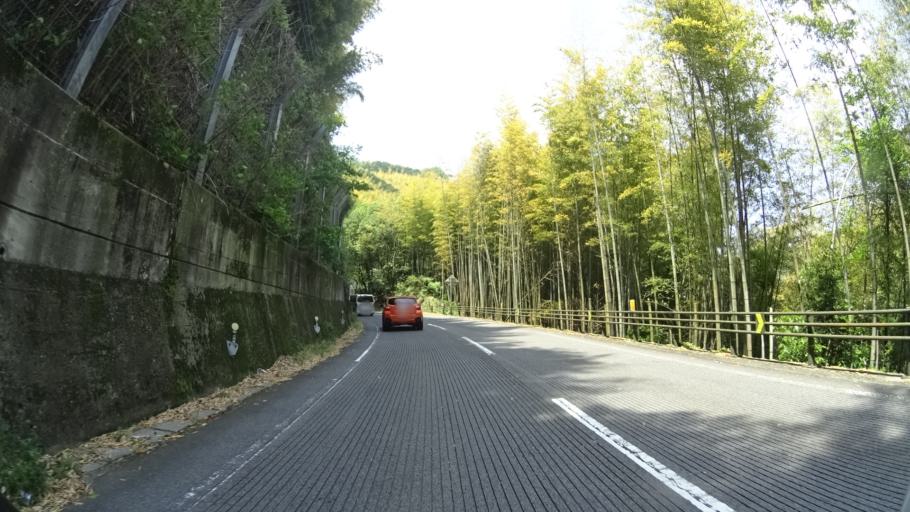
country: JP
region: Ehime
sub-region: Shikoku-chuo Shi
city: Matsuyama
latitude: 33.8772
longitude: 132.8362
